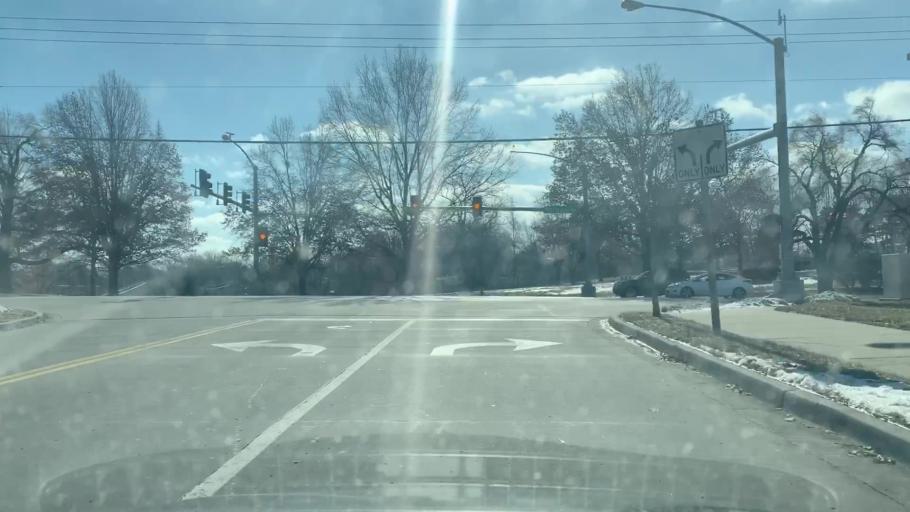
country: US
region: Missouri
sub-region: Clay County
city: Gladstone
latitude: 39.1815
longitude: -94.5731
